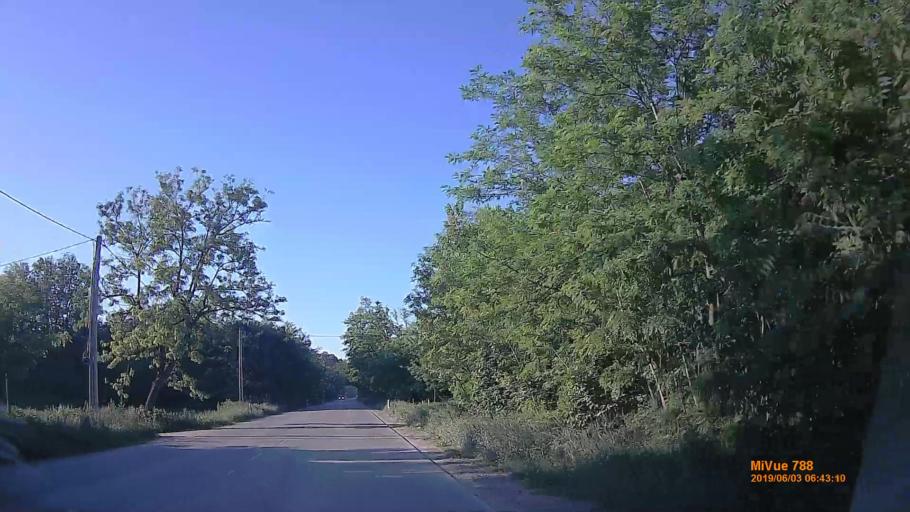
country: HU
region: Pest
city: Delegyhaza
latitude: 47.2584
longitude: 19.1222
